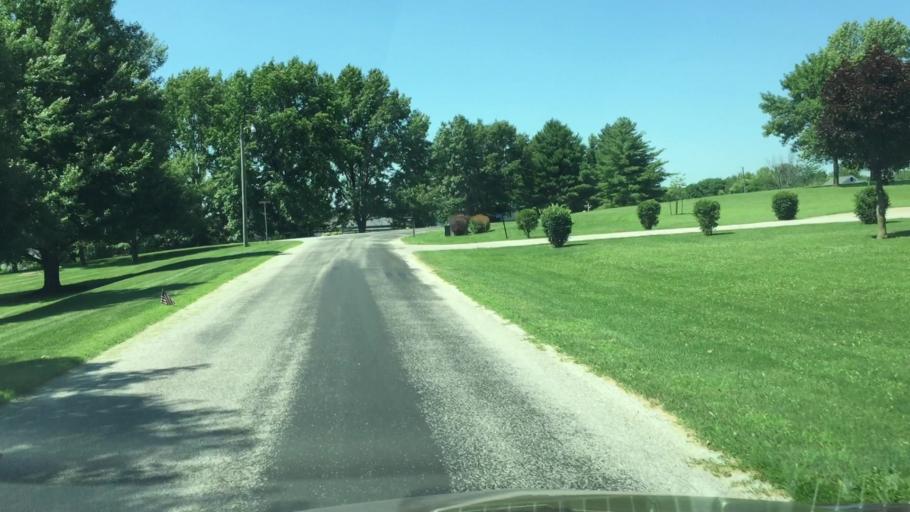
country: US
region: Iowa
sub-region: Johnson County
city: North Liberty
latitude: 41.8032
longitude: -91.6202
